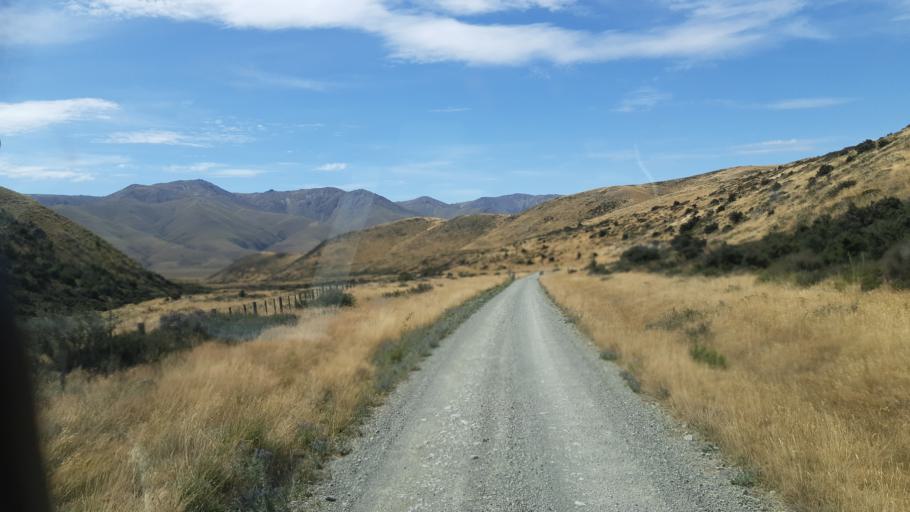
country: NZ
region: Canterbury
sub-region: Timaru District
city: Pleasant Point
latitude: -44.3524
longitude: 170.6057
